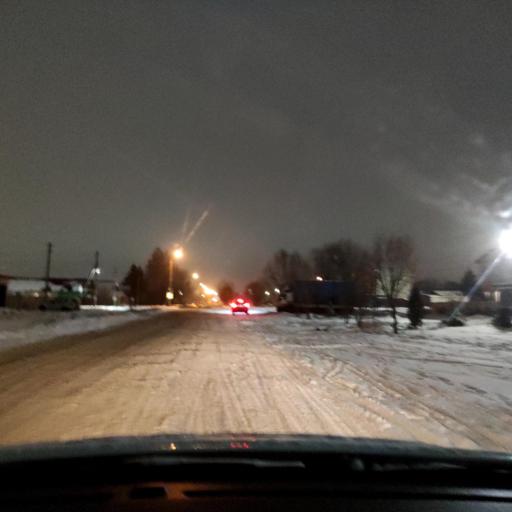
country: RU
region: Tatarstan
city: Staroye Arakchino
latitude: 55.8799
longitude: 49.0479
